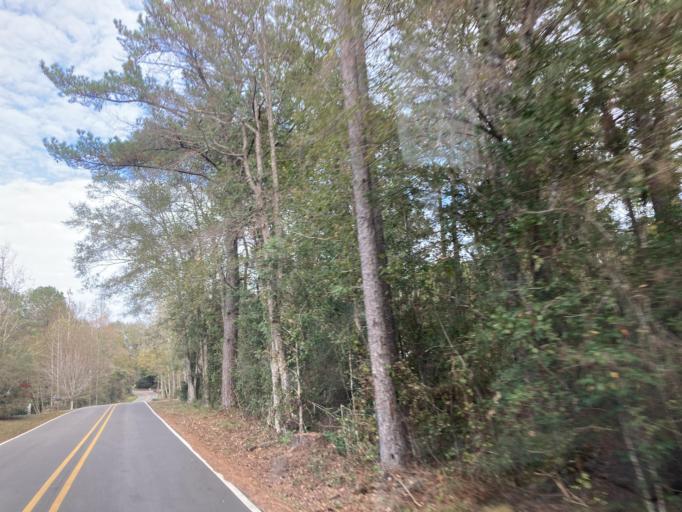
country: US
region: Mississippi
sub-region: Lamar County
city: Purvis
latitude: 31.2120
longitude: -89.3750
